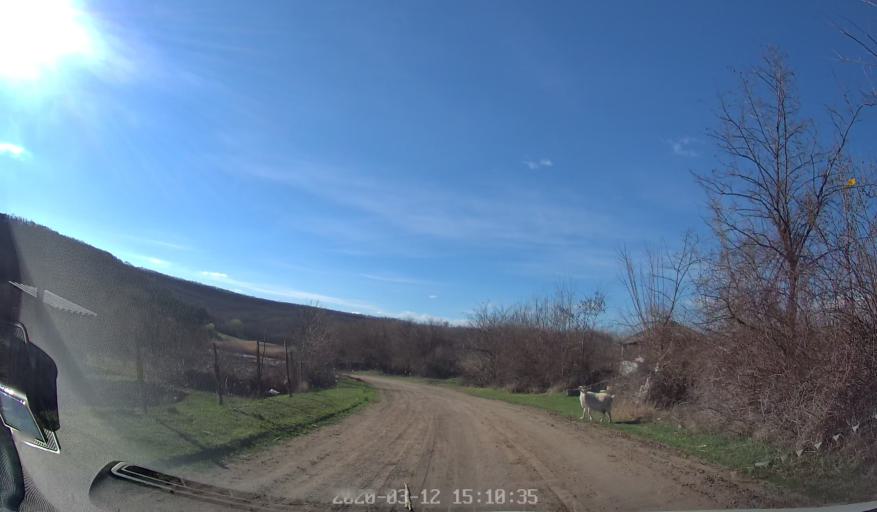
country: MD
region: Chisinau
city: Ciorescu
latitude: 47.2259
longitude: 28.9806
